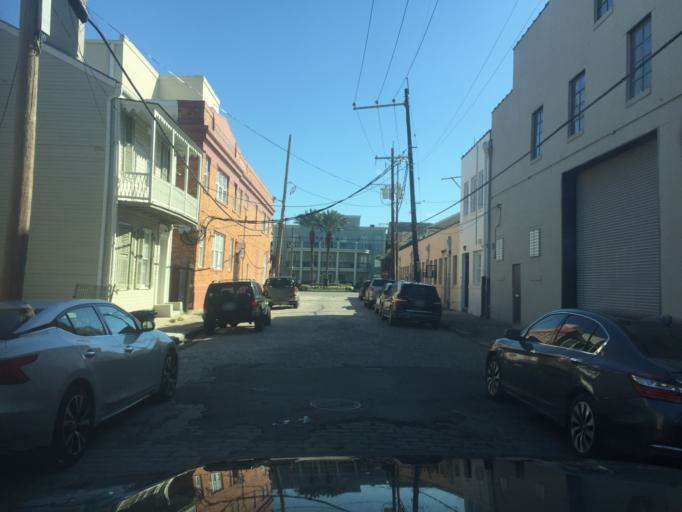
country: US
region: Louisiana
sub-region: Orleans Parish
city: New Orleans
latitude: 29.9359
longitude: -90.0702
